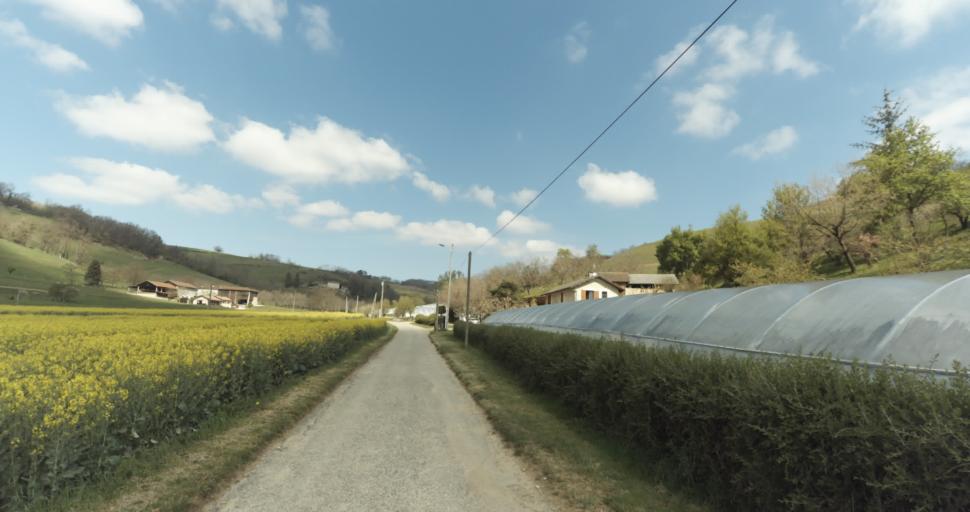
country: FR
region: Rhone-Alpes
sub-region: Departement de l'Isere
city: Saint-Verand
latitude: 45.1664
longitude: 5.3183
